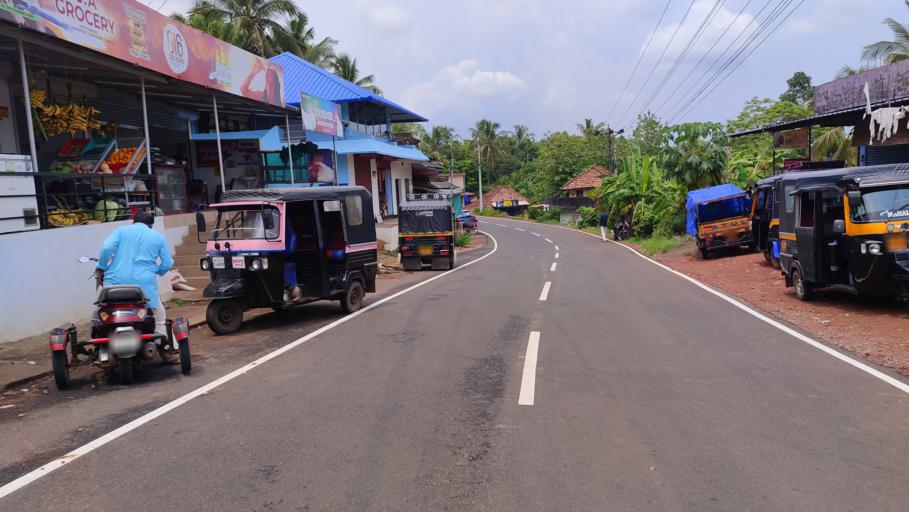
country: IN
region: Kerala
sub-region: Kasaragod District
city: Kannangad
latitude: 12.3166
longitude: 75.1455
